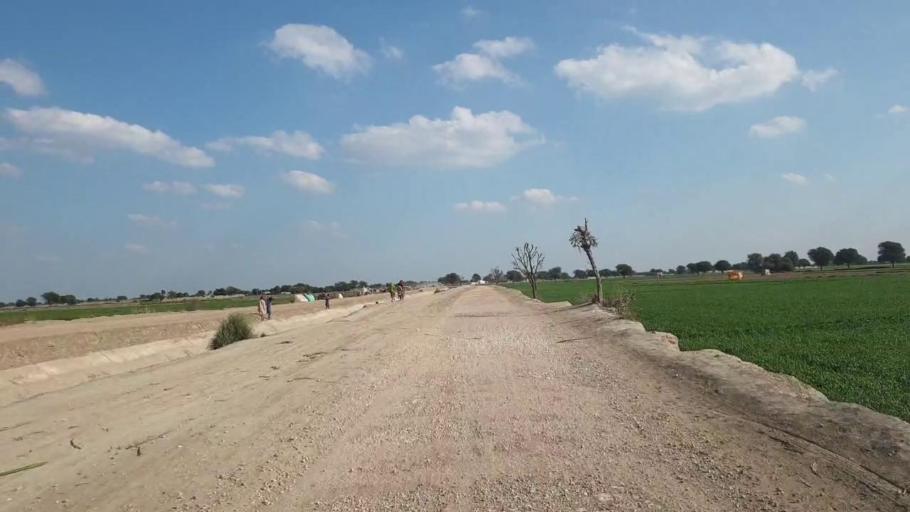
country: PK
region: Sindh
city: Shahpur Chakar
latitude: 26.1077
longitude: 68.5749
